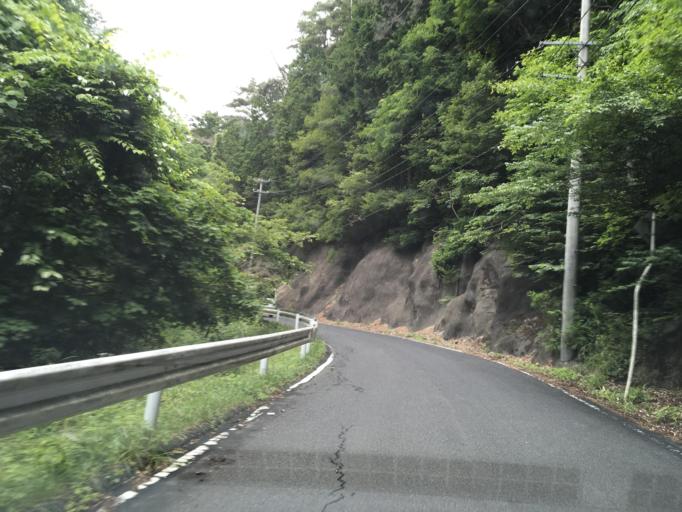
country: JP
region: Iwate
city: Ofunato
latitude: 38.9142
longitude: 141.6188
